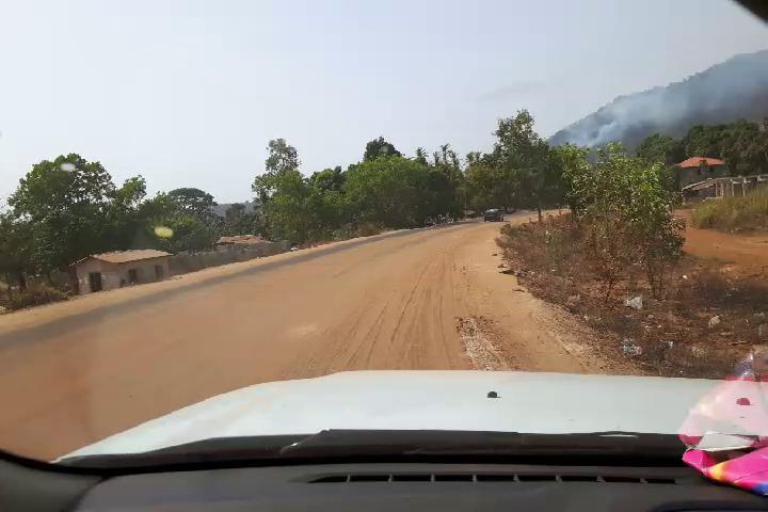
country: SL
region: Western Area
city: Waterloo
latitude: 8.2442
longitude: -13.1528
